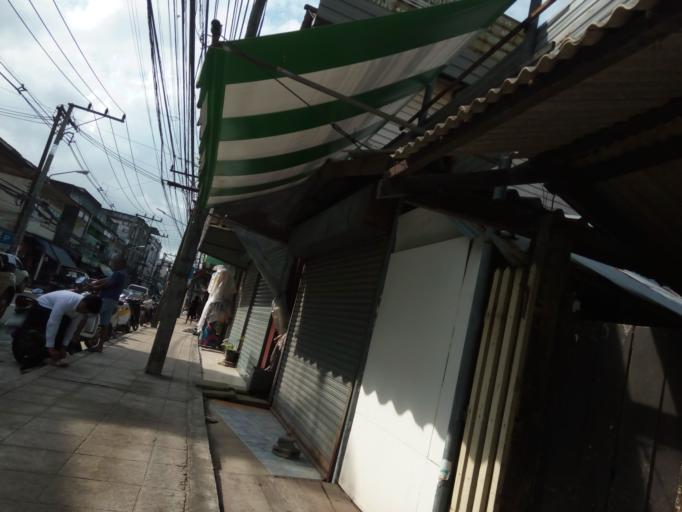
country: TH
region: Surat Thani
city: Ko Samui
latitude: 9.5344
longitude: 99.9359
